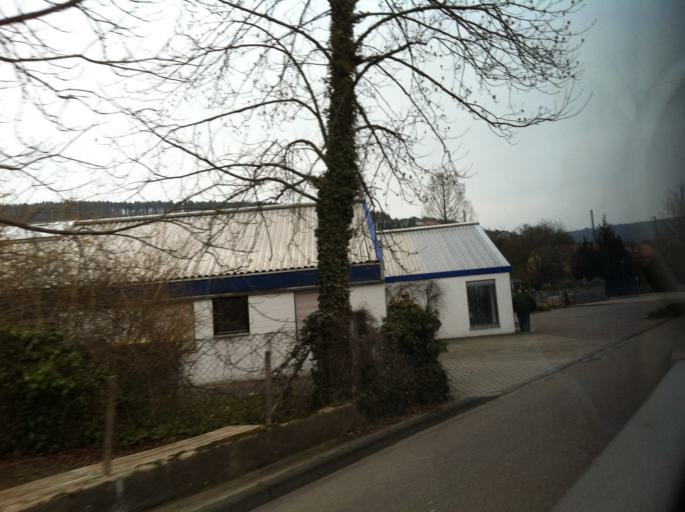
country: DE
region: Baden-Wuerttemberg
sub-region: Karlsruhe Region
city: Obrigheim
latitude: 49.3458
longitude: 9.1121
